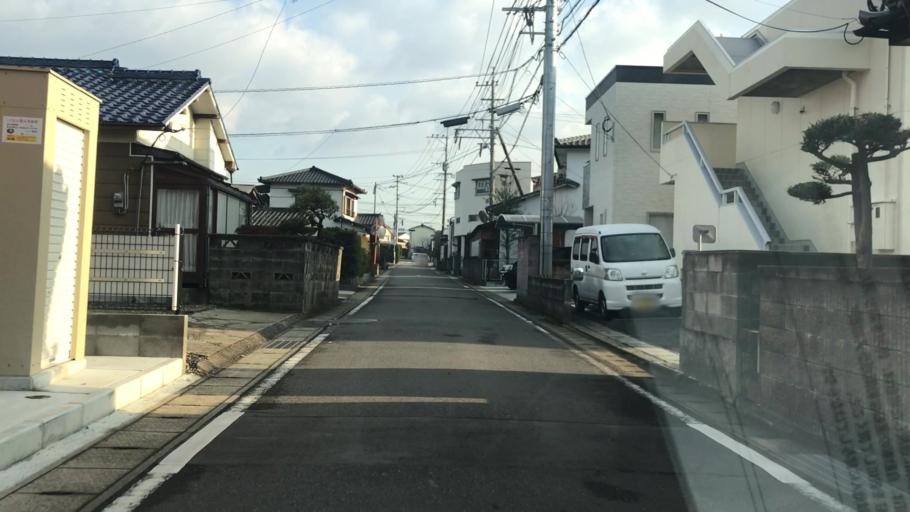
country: JP
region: Saga Prefecture
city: Takeocho-takeo
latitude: 33.1998
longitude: 130.0230
